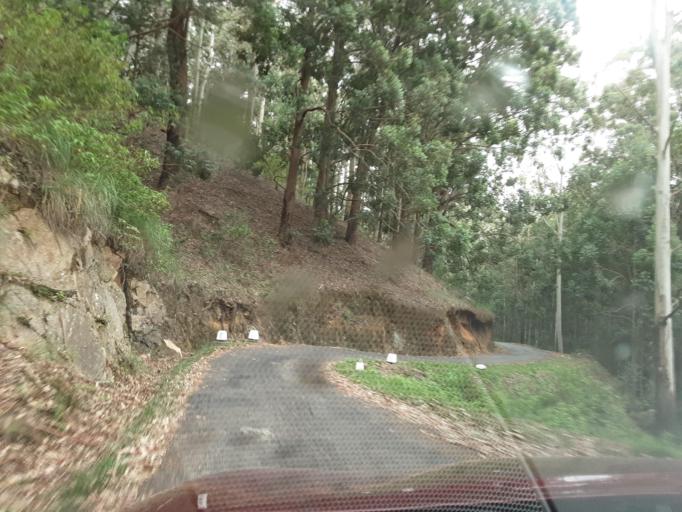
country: LK
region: Uva
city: Haputale
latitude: 6.8130
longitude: 80.8786
